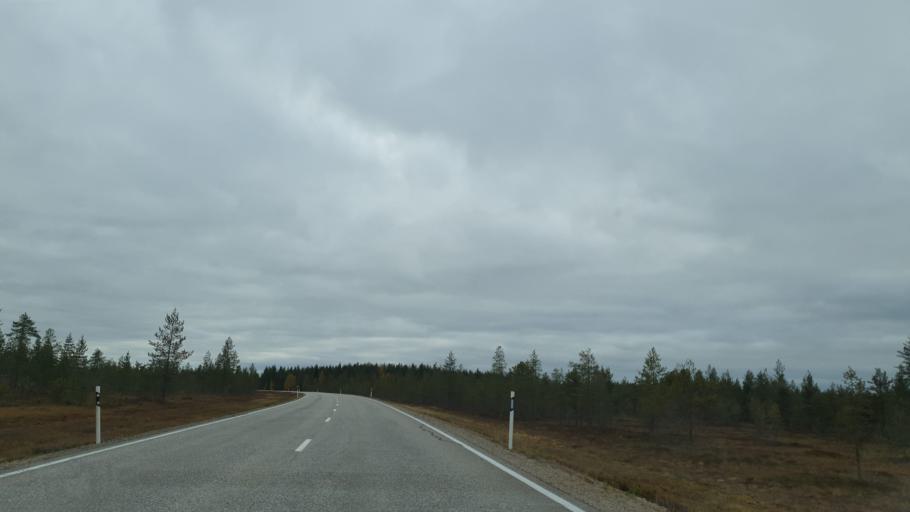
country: FI
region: Northern Ostrobothnia
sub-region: Oulunkaari
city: Pudasjaervi
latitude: 65.5954
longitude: 26.7214
